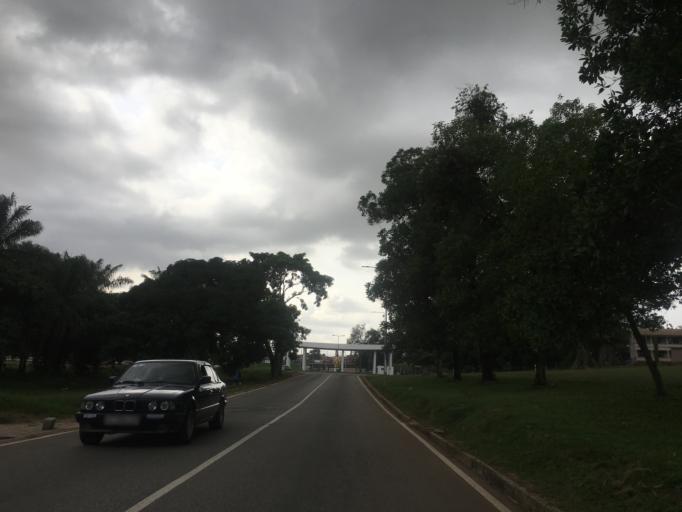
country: GH
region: Ashanti
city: Mamponteng
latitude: 6.6840
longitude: -1.5702
